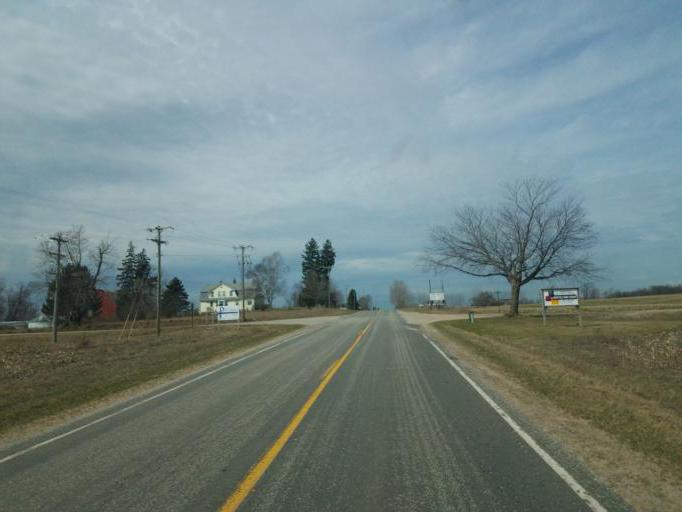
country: US
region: Michigan
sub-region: Oceana County
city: Shelby
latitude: 43.5589
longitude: -86.4363
